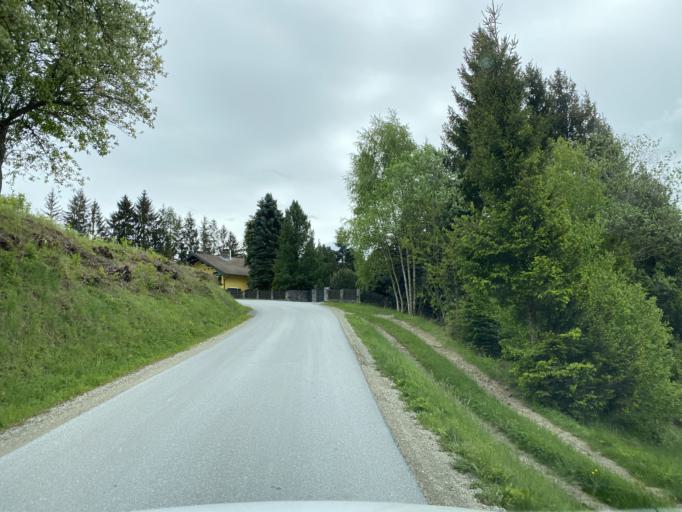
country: AT
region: Styria
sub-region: Politischer Bezirk Weiz
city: Koglhof
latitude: 47.3045
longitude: 15.7006
